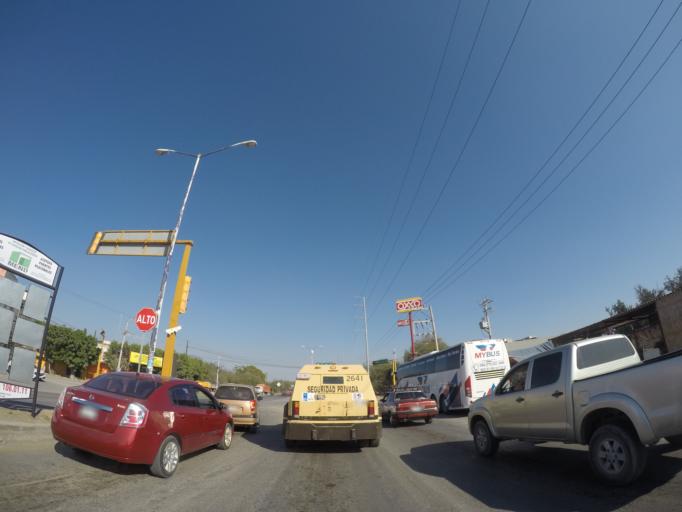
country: MX
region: San Luis Potosi
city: Rio Verde
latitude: 21.9225
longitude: -99.9812
